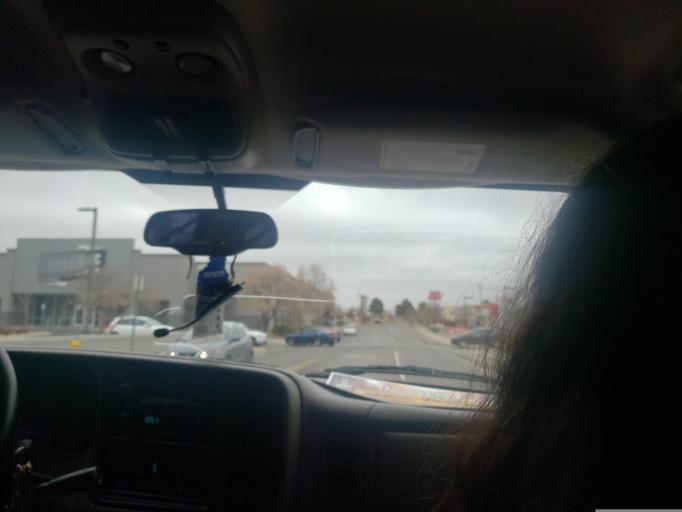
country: US
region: New Mexico
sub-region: Bernalillo County
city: Albuquerque
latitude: 35.1124
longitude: -106.7002
